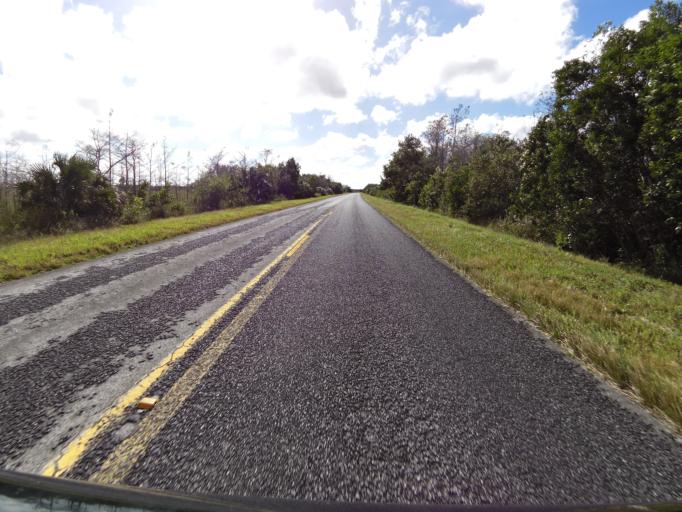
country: US
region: Florida
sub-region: Miami-Dade County
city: Florida City
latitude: 25.4025
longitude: -80.7909
